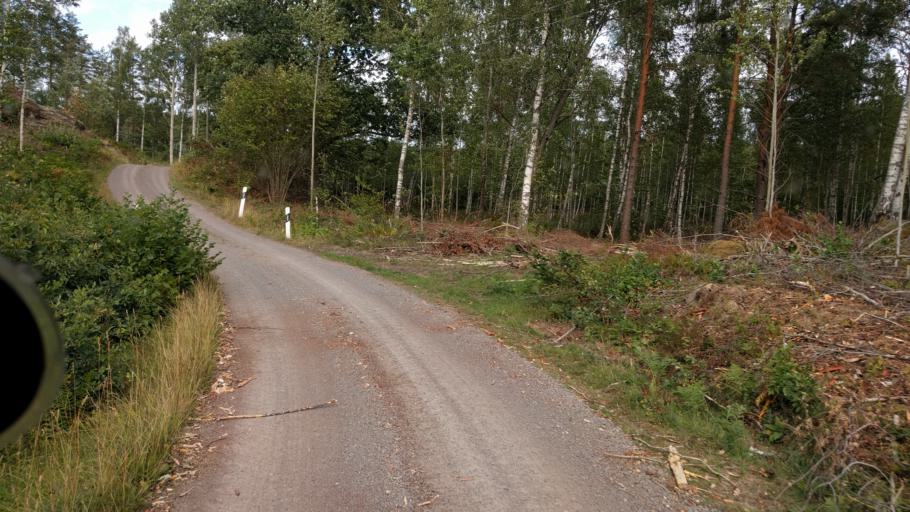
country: SE
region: Kalmar
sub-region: Vasterviks Kommun
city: Ankarsrum
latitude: 57.7274
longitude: 16.0944
